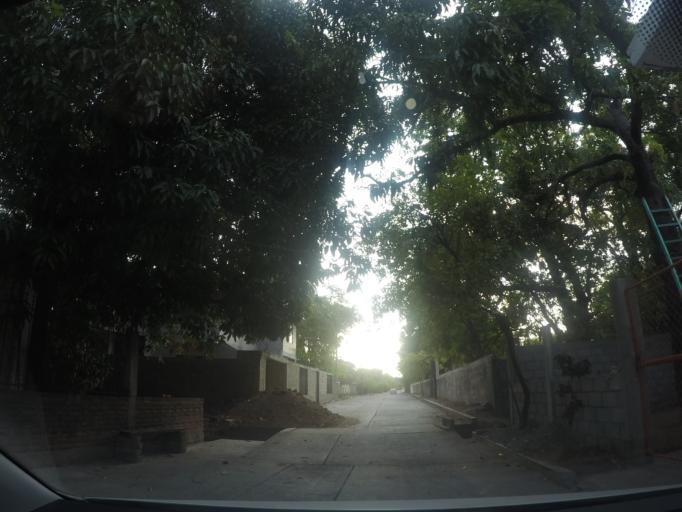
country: MX
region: Oaxaca
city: San Jeronimo Ixtepec
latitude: 16.5898
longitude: -95.1629
